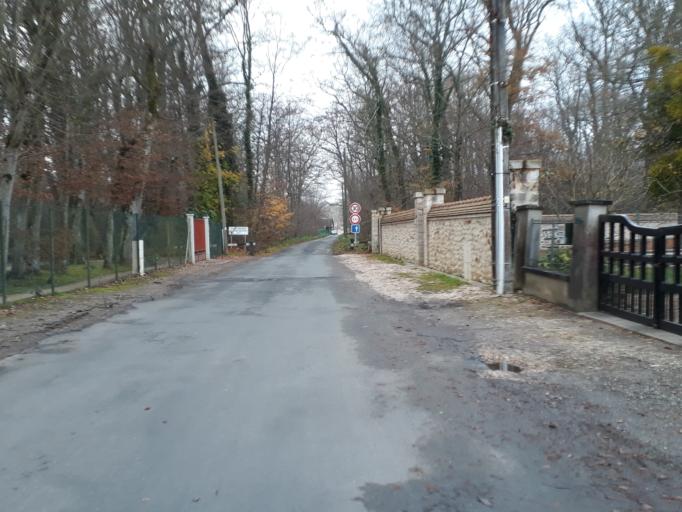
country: FR
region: Ile-de-France
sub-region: Departement de Seine-et-Marne
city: Bois-le-Roi
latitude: 48.4754
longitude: 2.6843
